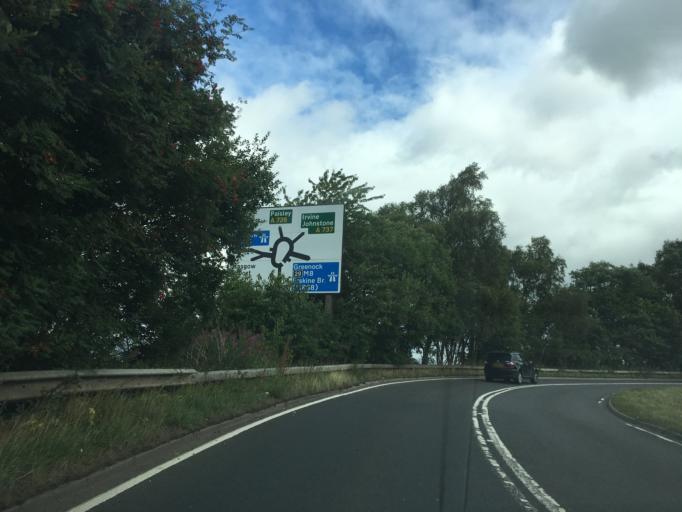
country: GB
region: Scotland
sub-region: Renfrewshire
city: Inchinnan
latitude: 55.8598
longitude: -4.4508
